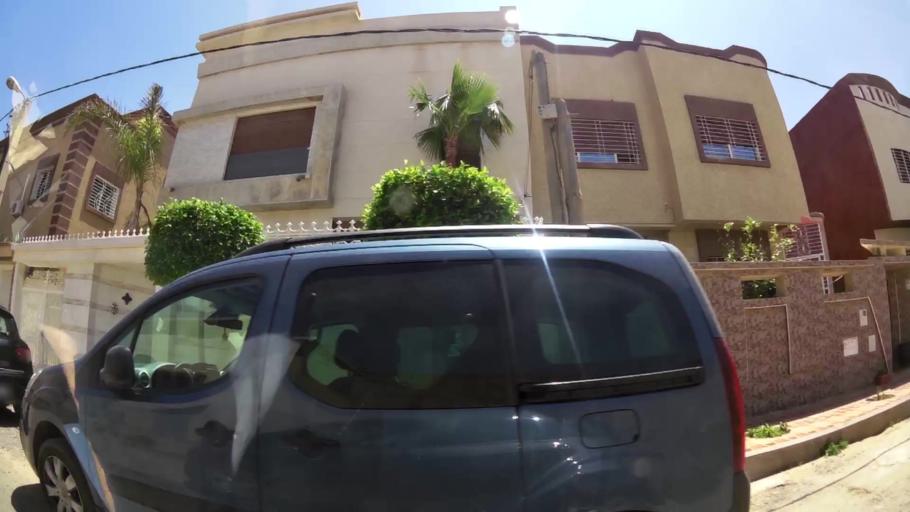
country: MA
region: Oriental
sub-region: Oujda-Angad
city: Oujda
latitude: 34.6657
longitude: -1.9444
